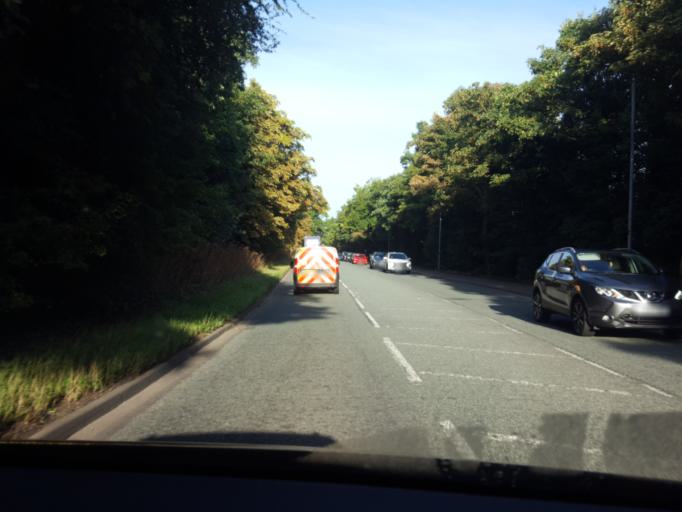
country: GB
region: England
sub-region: Leicestershire
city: Shepshed
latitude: 52.7599
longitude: -1.2809
